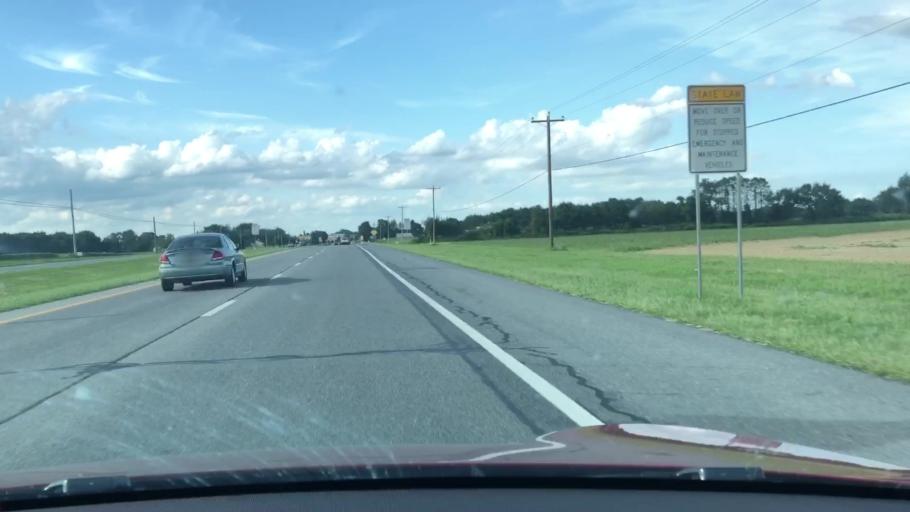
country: US
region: Delaware
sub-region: Kent County
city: Felton
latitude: 38.9990
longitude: -75.5688
